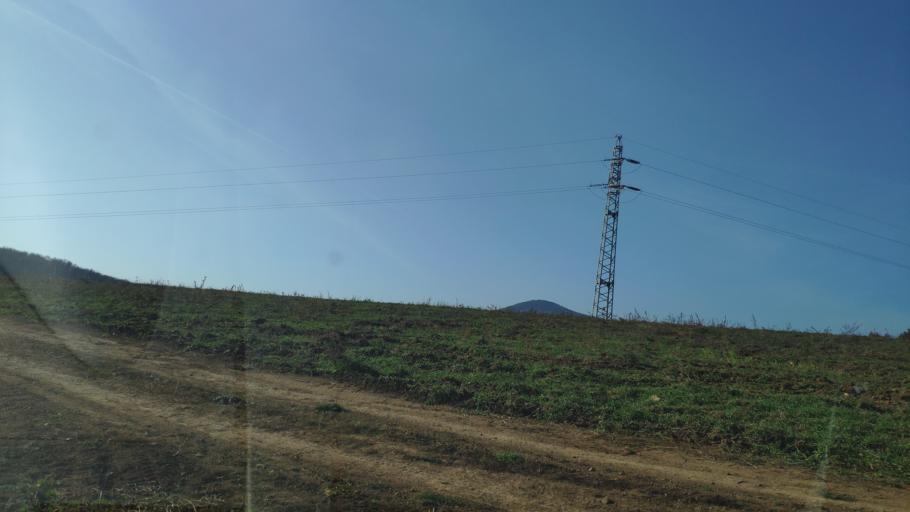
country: SK
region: Presovsky
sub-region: Okres Presov
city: Presov
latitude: 48.8944
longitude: 21.2272
